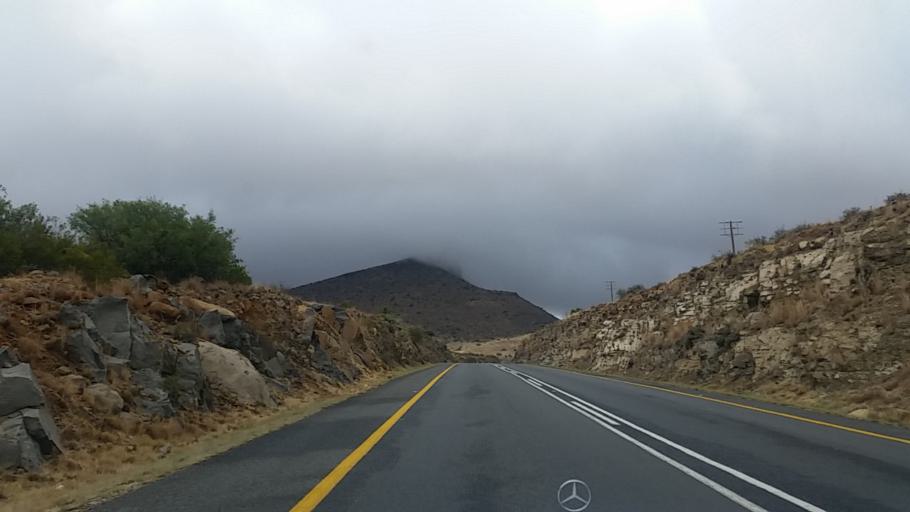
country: ZA
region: Eastern Cape
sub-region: Cacadu District Municipality
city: Graaff-Reinet
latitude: -32.1074
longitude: 24.6073
